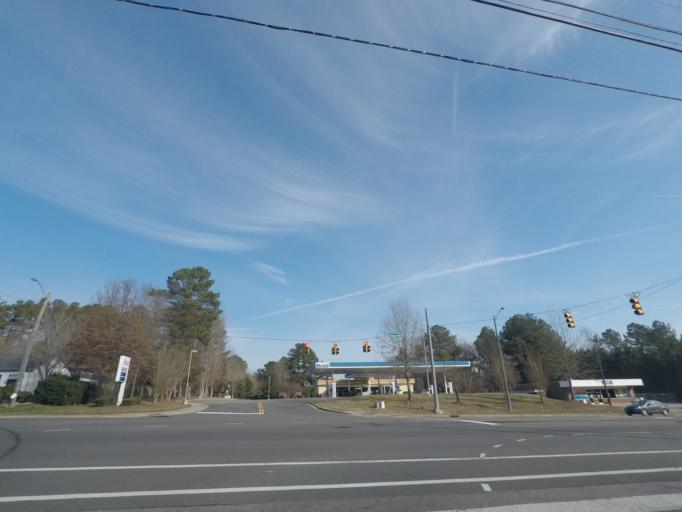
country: US
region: North Carolina
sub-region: Durham County
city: Durham
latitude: 36.0831
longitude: -78.9318
